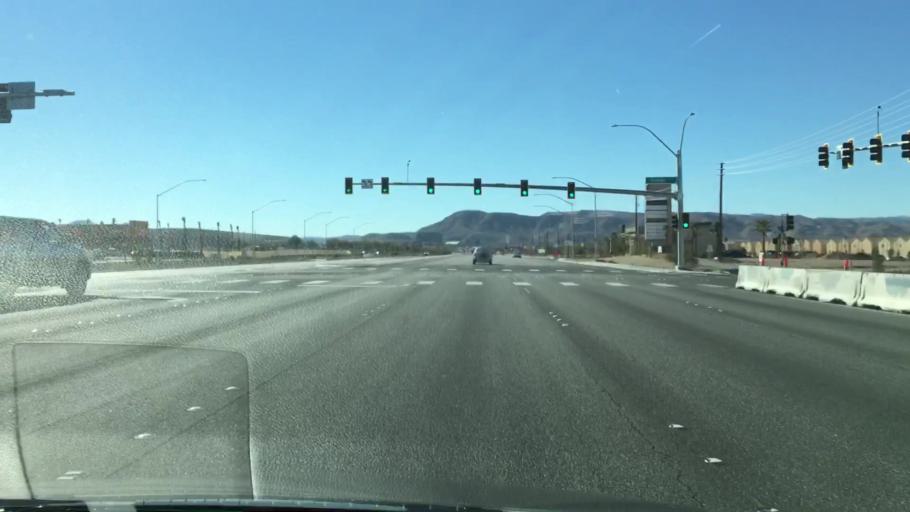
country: US
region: Nevada
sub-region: Clark County
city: Whitney
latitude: 35.9883
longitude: -115.1409
